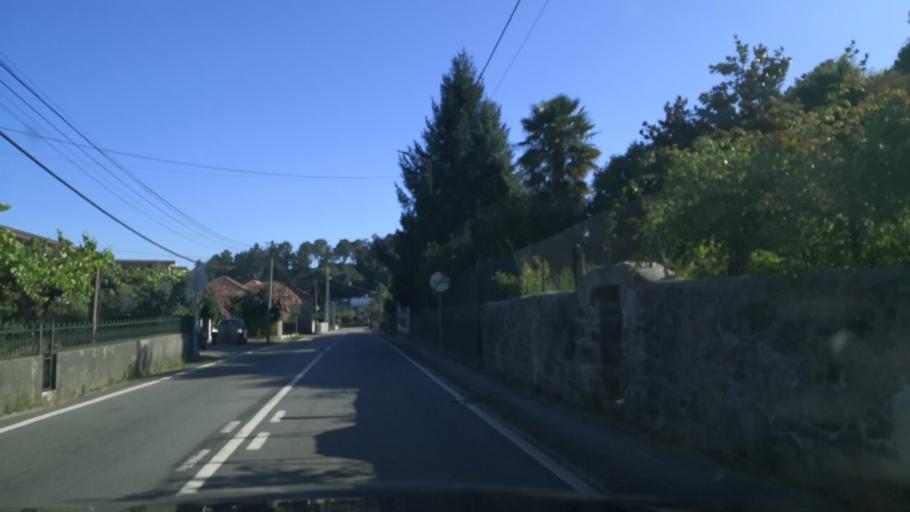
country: PT
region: Porto
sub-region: Santo Tirso
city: Sao Miguel do Couto
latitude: 41.2888
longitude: -8.4713
